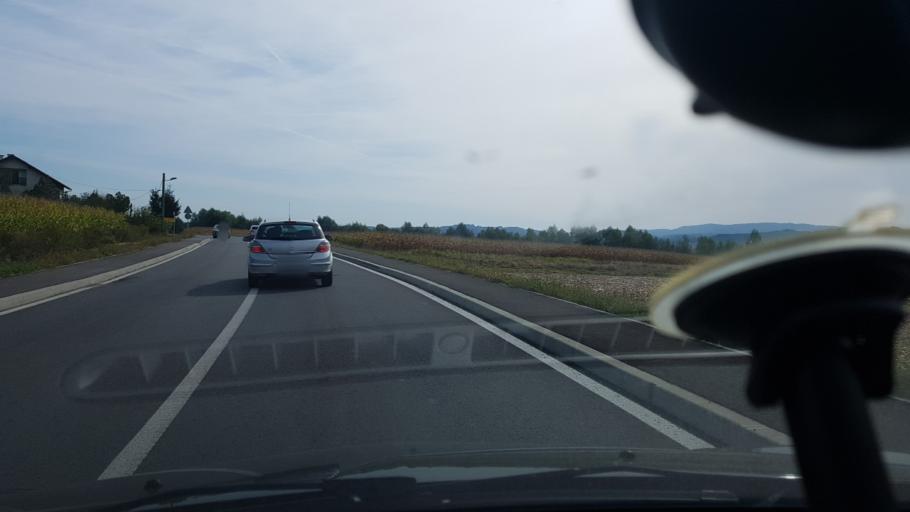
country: HR
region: Krapinsko-Zagorska
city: Marija Bistrica
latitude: 46.0515
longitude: 16.1245
